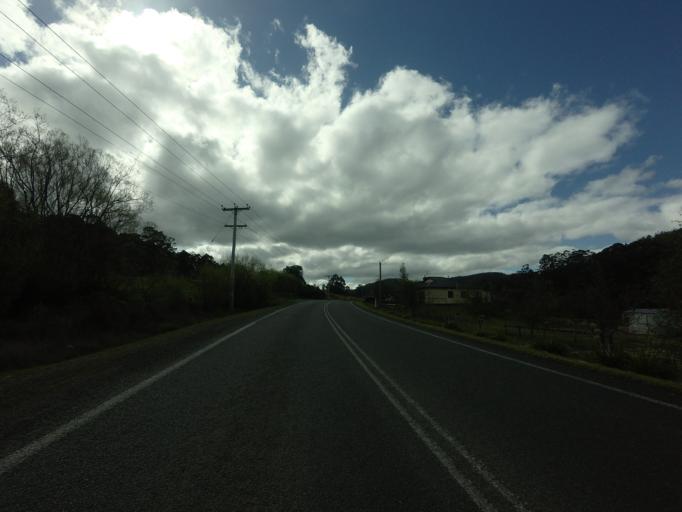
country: AU
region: Tasmania
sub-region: Huon Valley
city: Geeveston
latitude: -43.3020
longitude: 147.0073
